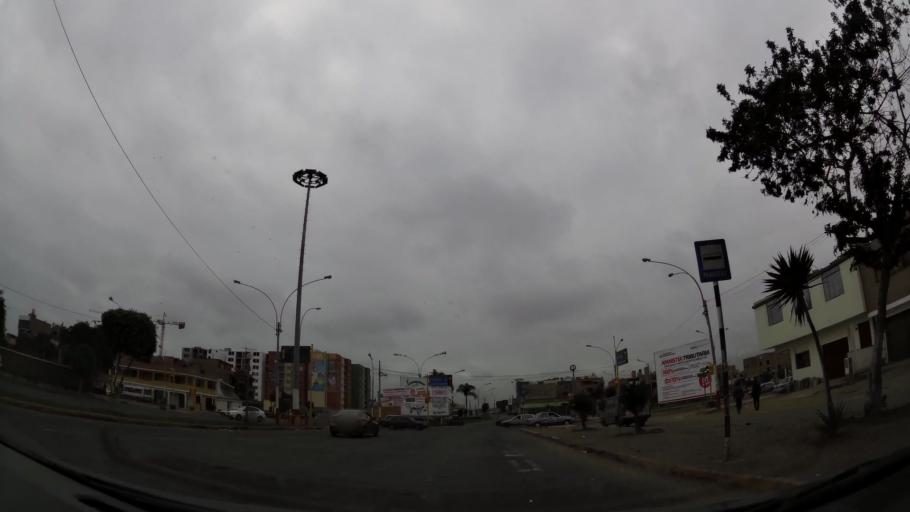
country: PE
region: Callao
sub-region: Callao
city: Callao
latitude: -12.0539
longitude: -77.1150
